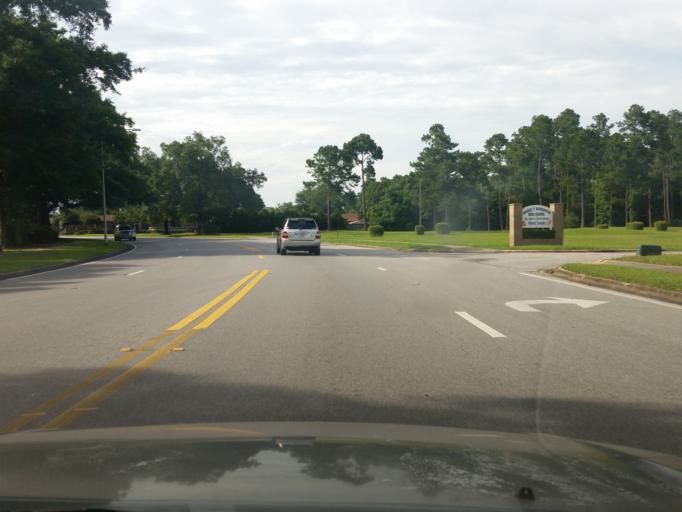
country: US
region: Florida
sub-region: Escambia County
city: Ferry Pass
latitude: 30.4847
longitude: -87.2135
